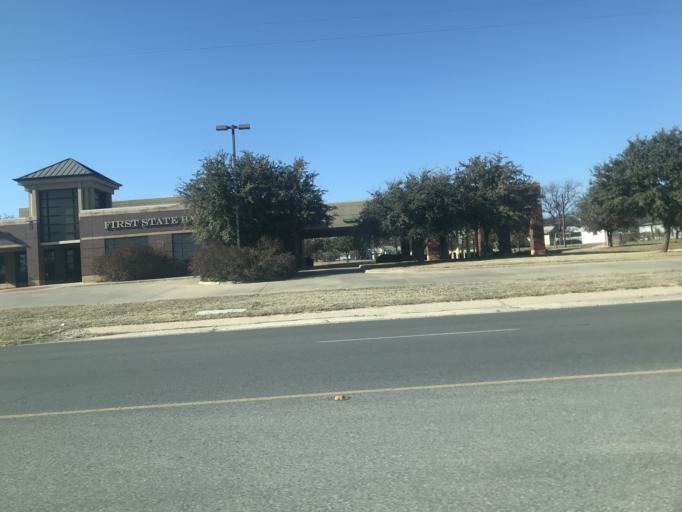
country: US
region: Texas
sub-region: Taylor County
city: Abilene
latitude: 32.4224
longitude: -99.7362
